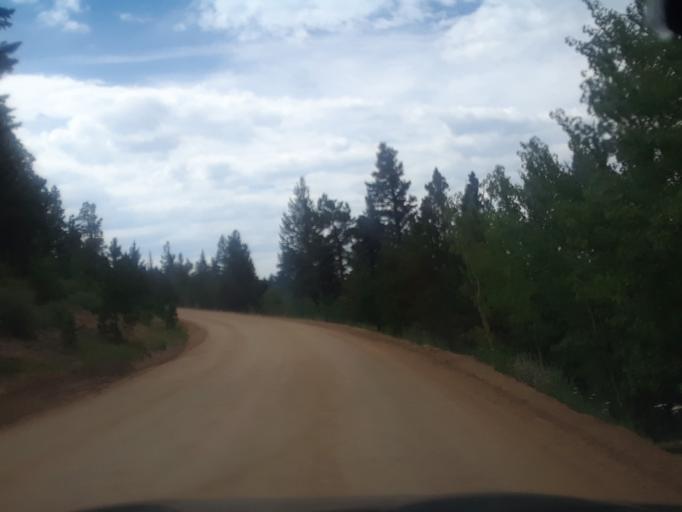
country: US
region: Colorado
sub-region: Boulder County
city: Nederland
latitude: 40.0444
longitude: -105.5168
